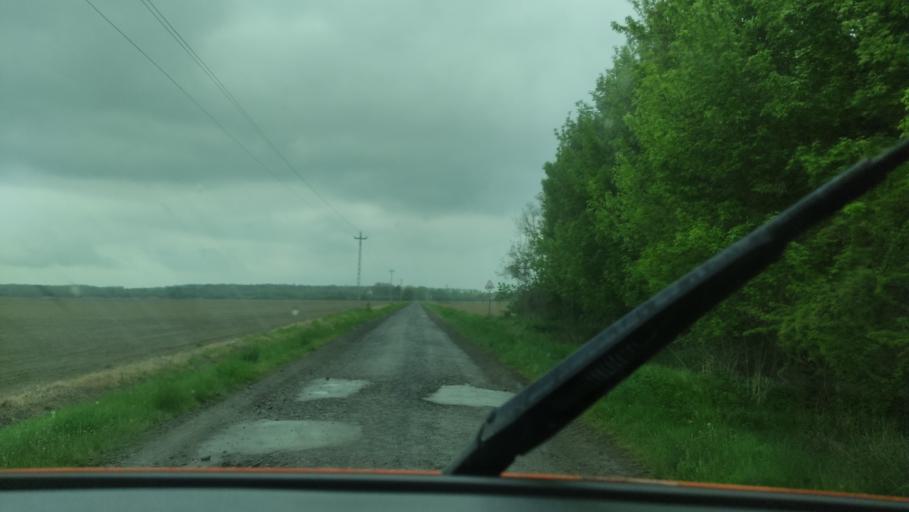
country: HR
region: Osjecko-Baranjska
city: Batina
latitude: 45.9017
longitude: 18.7746
